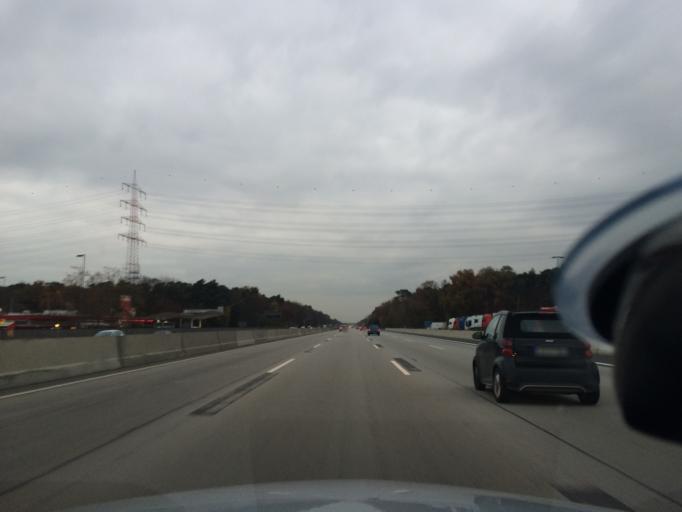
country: DE
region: Hesse
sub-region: Regierungsbezirk Darmstadt
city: Erzhausen
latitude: 49.9461
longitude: 8.6103
